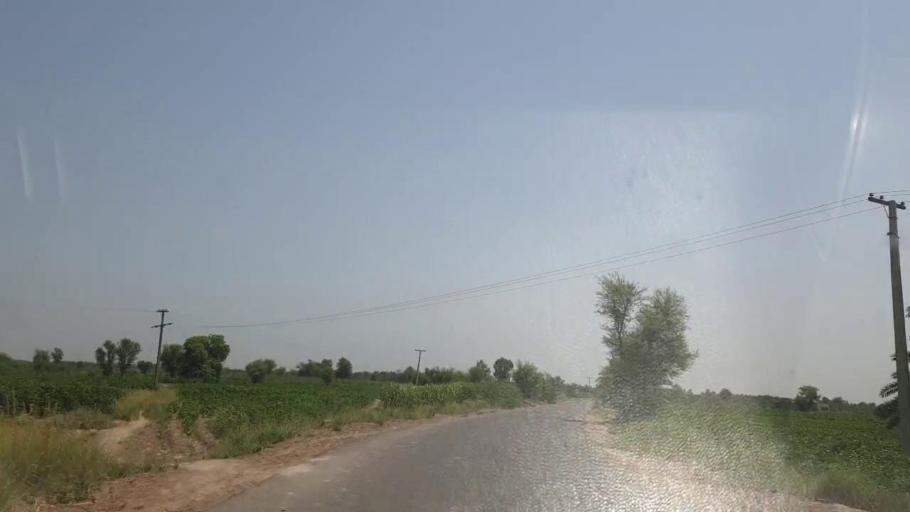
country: PK
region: Sindh
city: Bozdar
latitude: 27.2823
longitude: 68.6233
